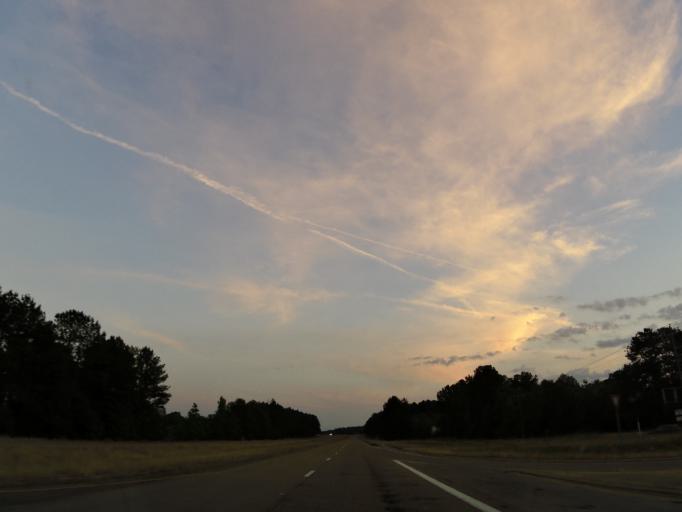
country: US
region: Mississippi
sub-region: Kemper County
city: De Kalb
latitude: 32.6935
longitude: -88.4869
